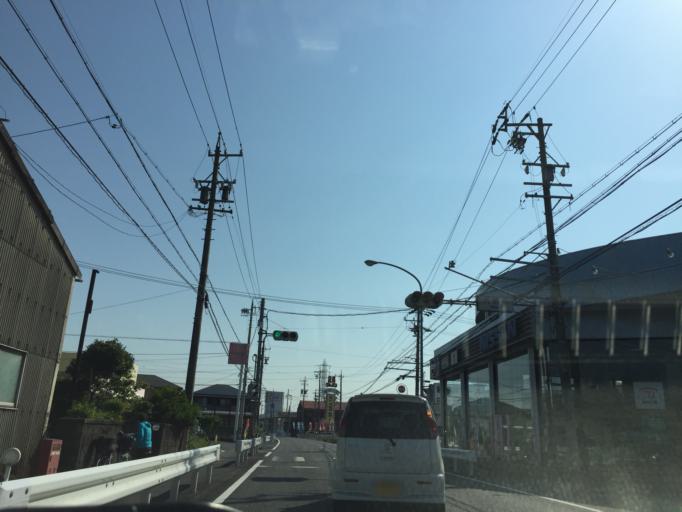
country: JP
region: Mie
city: Yokkaichi
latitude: 34.9909
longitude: 136.6410
